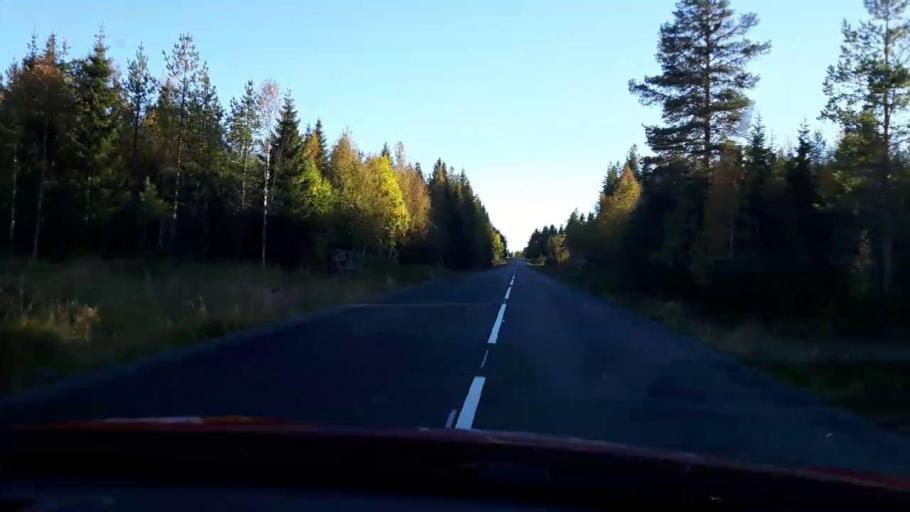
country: SE
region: Jaemtland
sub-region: OEstersunds Kommun
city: Lit
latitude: 63.5398
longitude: 14.8507
